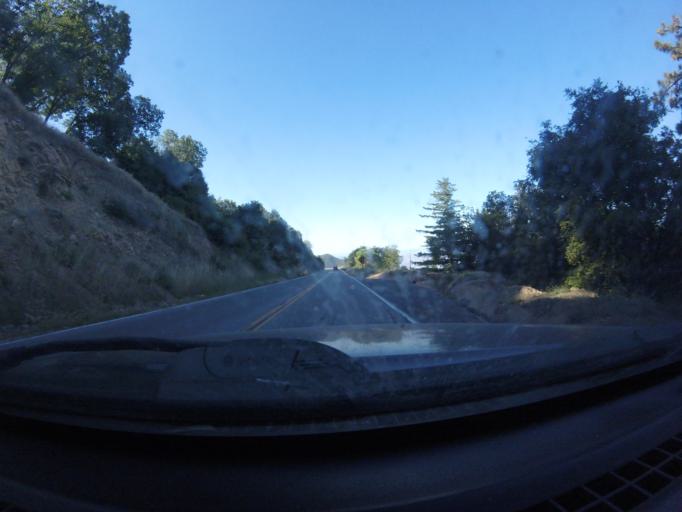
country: US
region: California
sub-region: San Bernardino County
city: Running Springs
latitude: 34.1994
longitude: -117.1530
